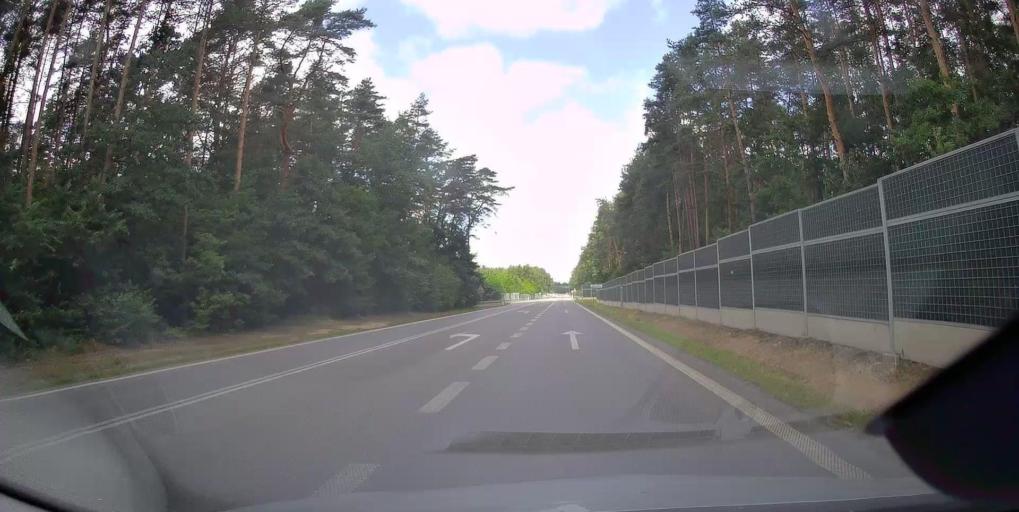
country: PL
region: Subcarpathian Voivodeship
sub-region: Powiat mielecki
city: Mielec
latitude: 50.2866
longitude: 21.4970
